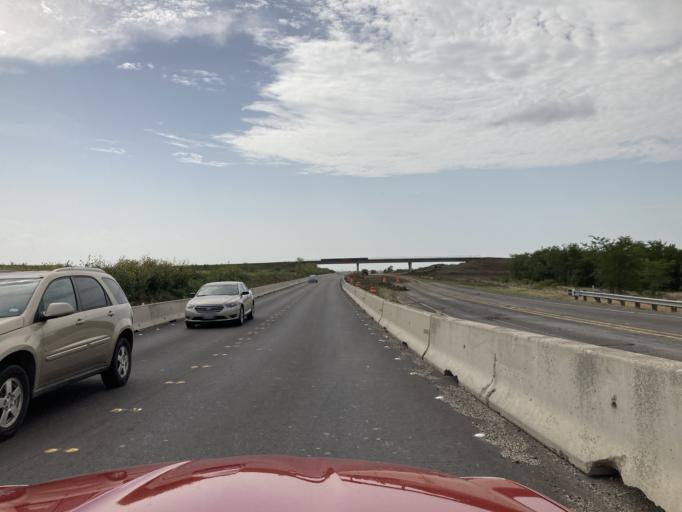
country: US
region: Texas
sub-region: Navarro County
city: Corsicana
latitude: 32.0474
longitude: -96.4173
